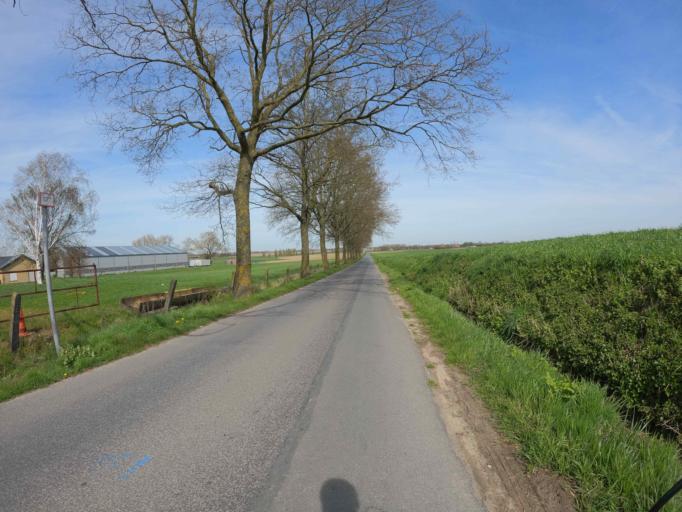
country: BE
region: Flanders
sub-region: Provincie West-Vlaanderen
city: Tielt
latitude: 51.0060
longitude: 3.3387
